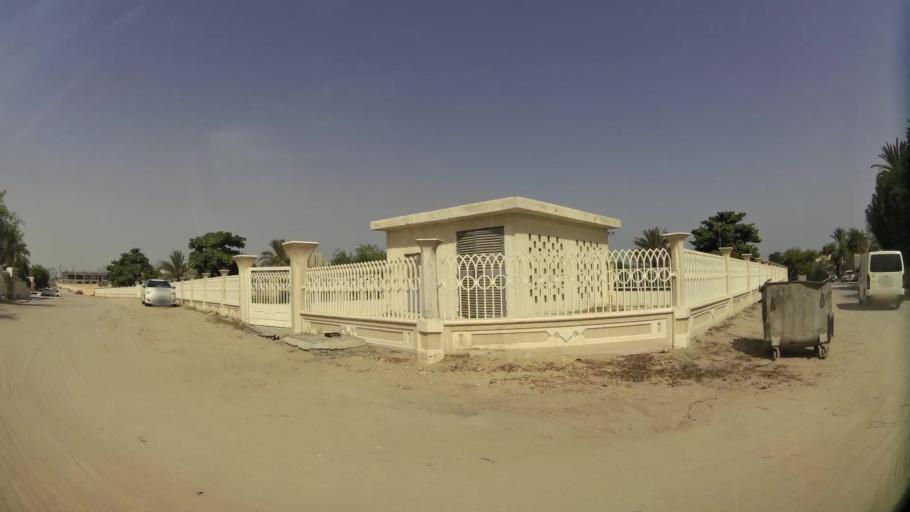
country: AE
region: Ash Shariqah
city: Sharjah
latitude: 25.3488
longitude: 55.4153
